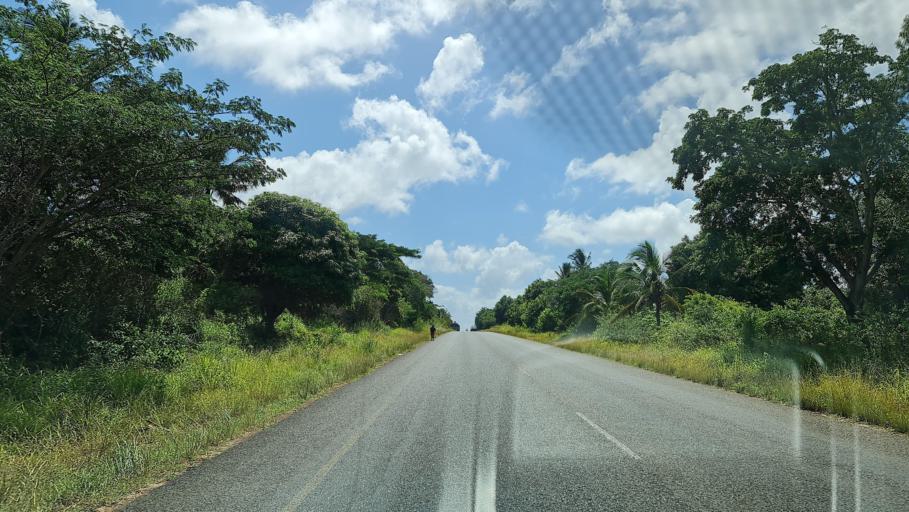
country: MZ
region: Inhambane
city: Maxixe
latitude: -24.5354
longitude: 34.9415
